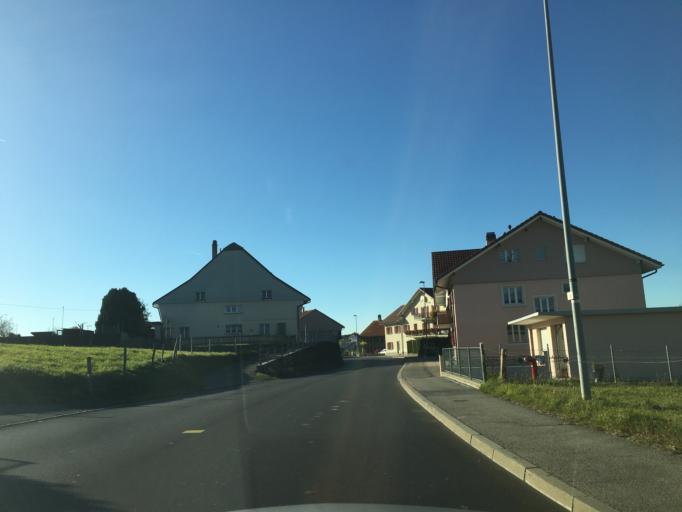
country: CH
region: Fribourg
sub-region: Gruyere District
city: Sales
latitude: 46.6206
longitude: 6.9934
